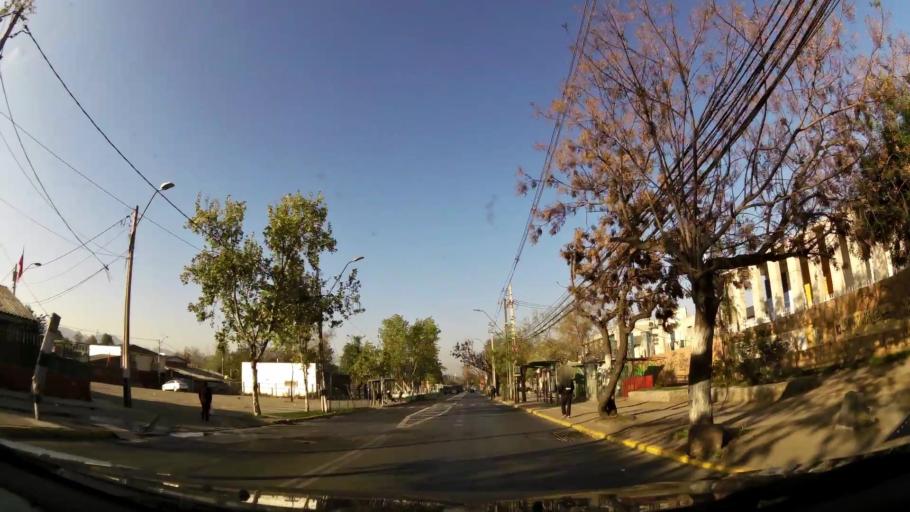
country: CL
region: Santiago Metropolitan
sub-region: Provincia de Santiago
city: Santiago
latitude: -33.3729
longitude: -70.6364
